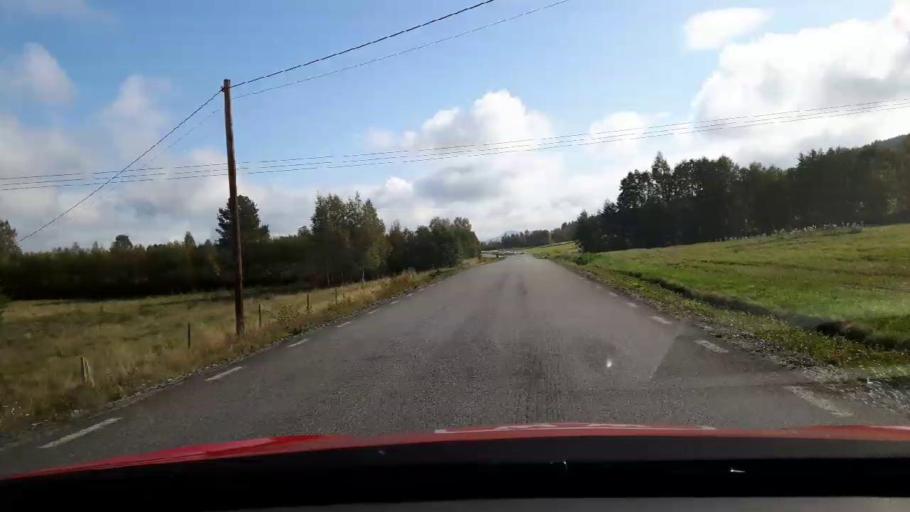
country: SE
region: Gaevleborg
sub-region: Ljusdals Kommun
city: Ljusdal
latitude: 61.7647
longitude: 16.0531
